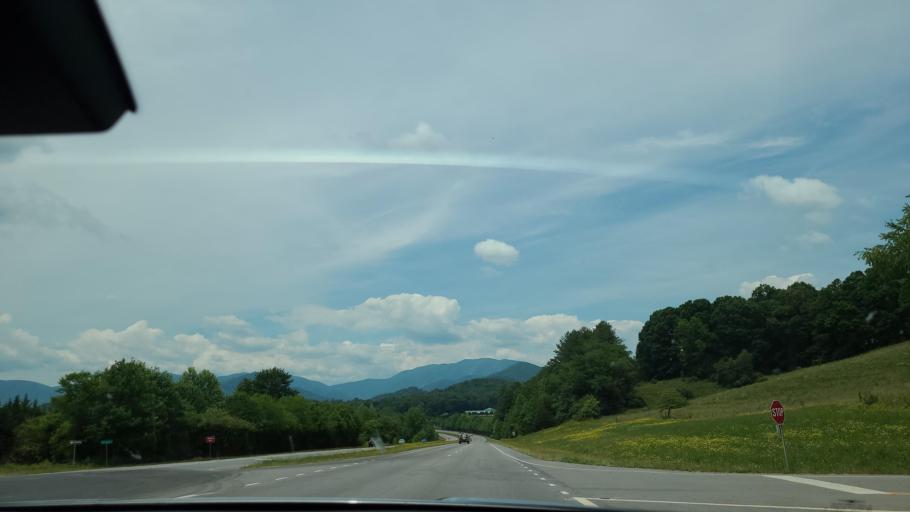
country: US
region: North Carolina
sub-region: Macon County
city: Franklin
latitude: 35.1649
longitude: -83.4237
